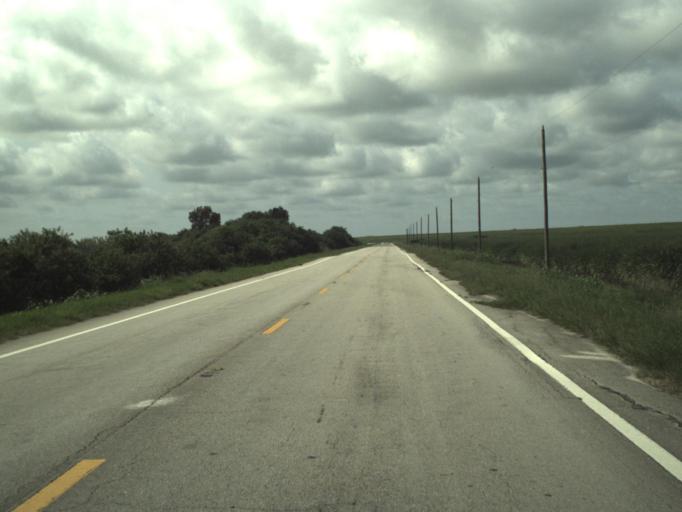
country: US
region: Florida
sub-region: Palm Beach County
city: Pahokee
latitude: 26.7754
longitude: -80.6892
